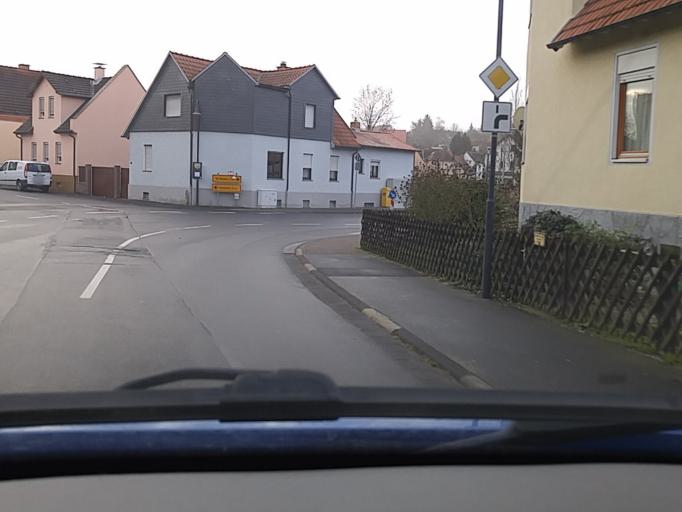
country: DE
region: Hesse
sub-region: Regierungsbezirk Darmstadt
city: Bad Nauheim
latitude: 50.3668
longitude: 8.7637
